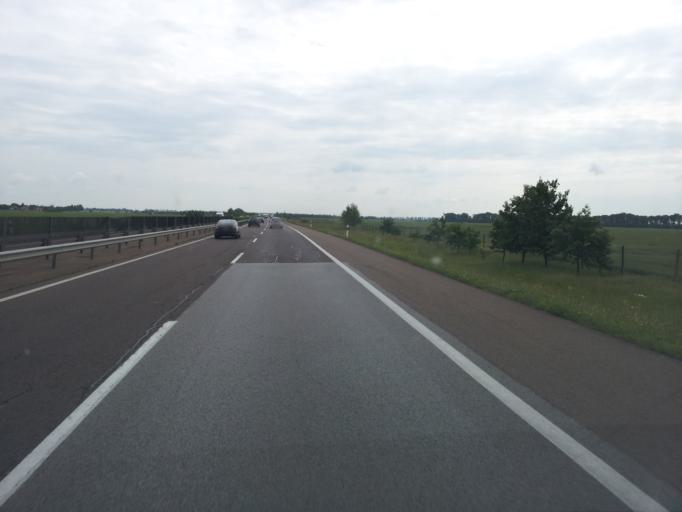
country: HU
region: Heves
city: Szihalom
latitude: 47.7566
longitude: 20.4824
